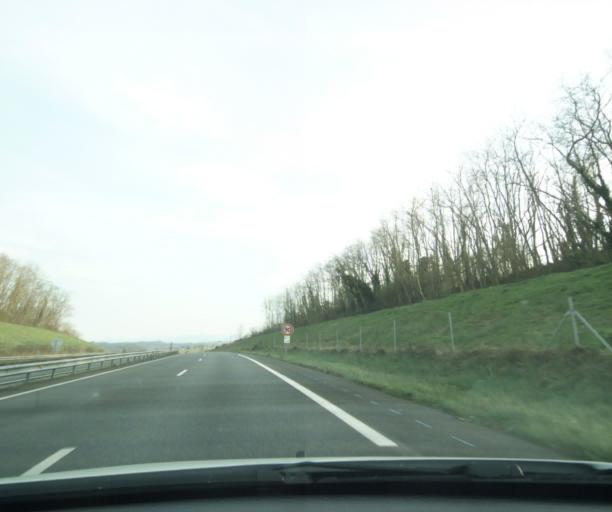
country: FR
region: Midi-Pyrenees
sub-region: Departement des Hautes-Pyrenees
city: Barbazan-Debat
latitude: 43.2023
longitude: 0.1481
